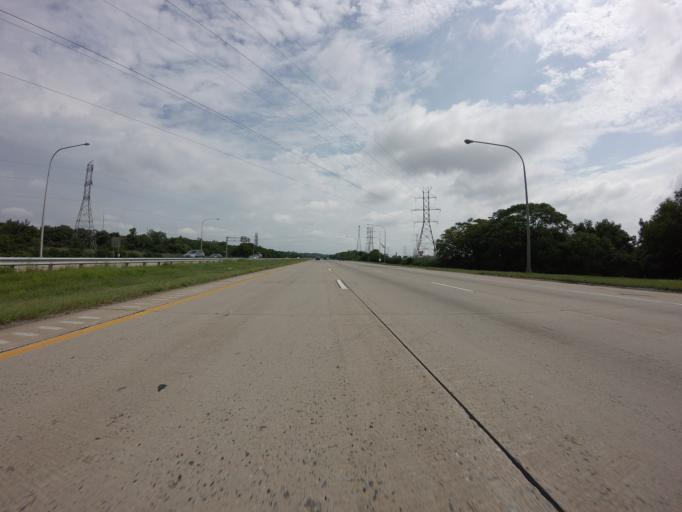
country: US
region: Delaware
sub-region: New Castle County
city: Edgemoor
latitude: 39.7377
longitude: -75.5196
